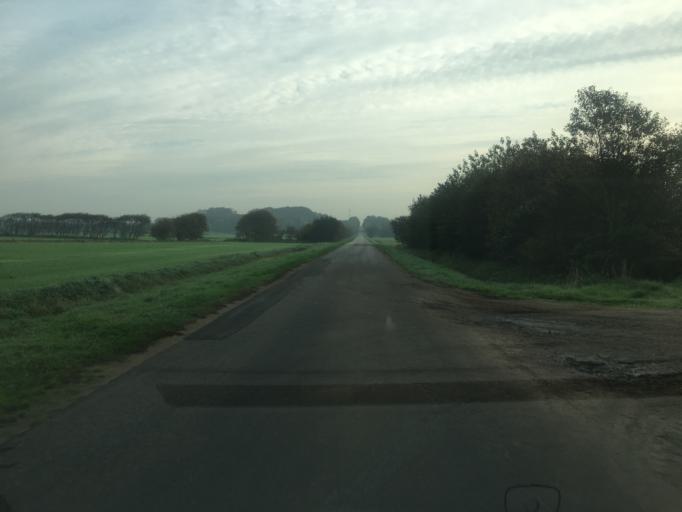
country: DK
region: South Denmark
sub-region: Tonder Kommune
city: Toftlund
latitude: 55.1029
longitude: 9.0739
